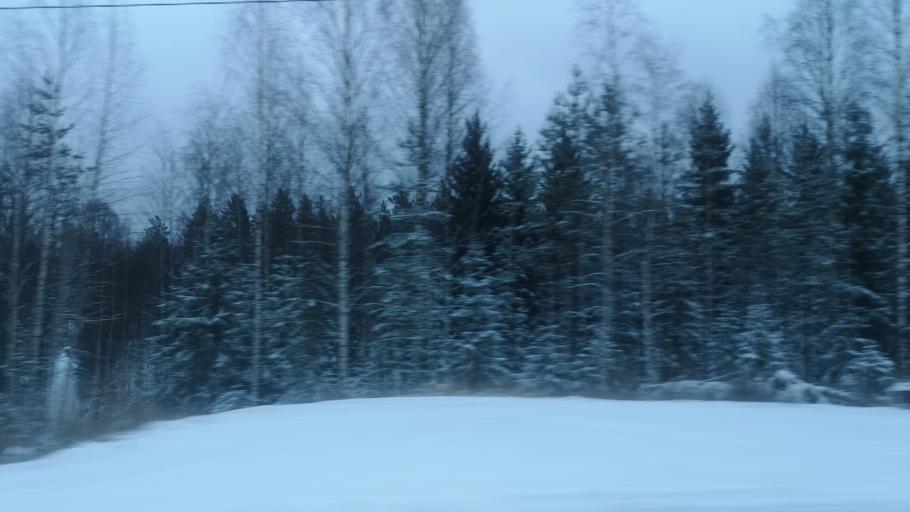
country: FI
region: Southern Savonia
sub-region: Savonlinna
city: Enonkoski
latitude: 62.0524
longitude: 28.7040
